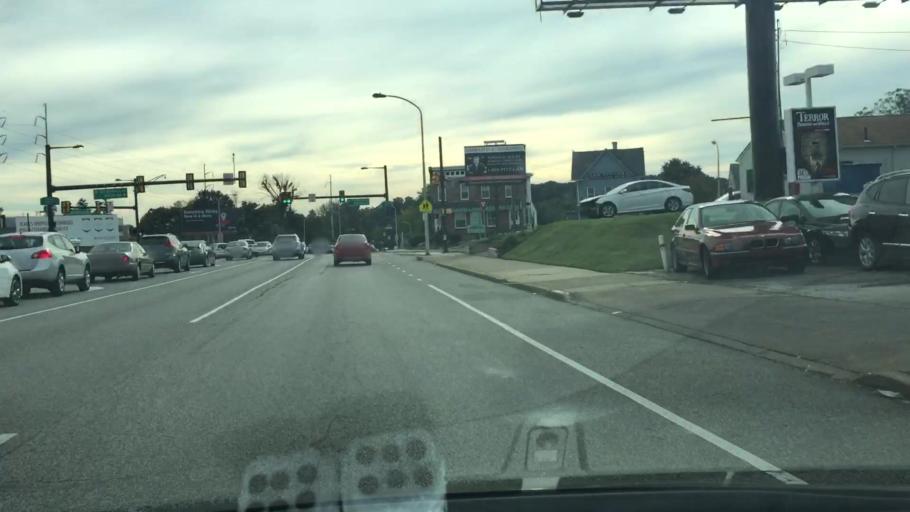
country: US
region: Pennsylvania
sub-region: Montgomery County
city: Rockledge
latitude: 40.0852
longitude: -75.0378
